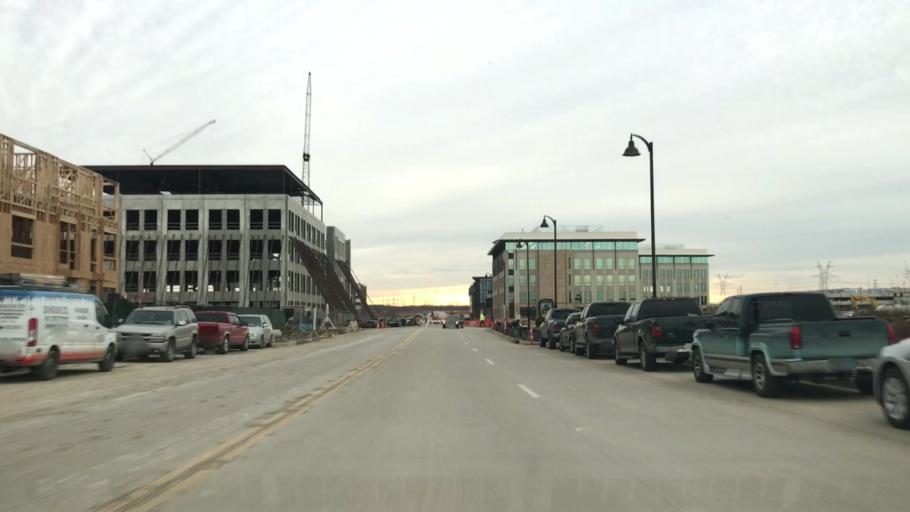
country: US
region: Texas
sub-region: Dallas County
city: Coppell
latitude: 32.9372
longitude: -96.9862
